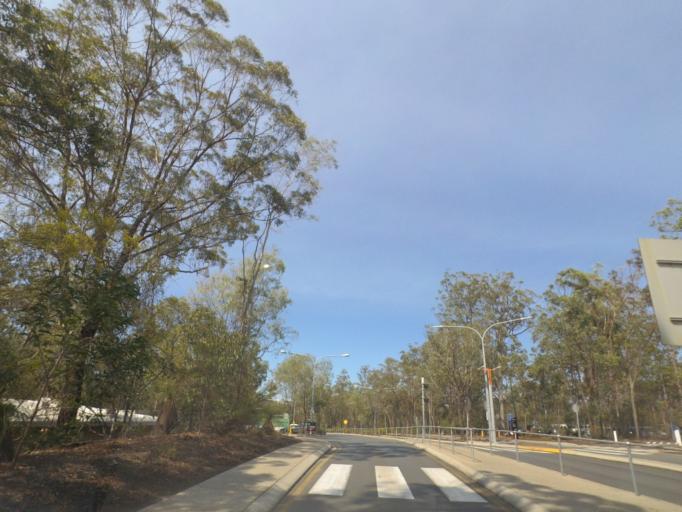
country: AU
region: Queensland
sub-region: Brisbane
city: Nathan
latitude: -27.5539
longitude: 153.0559
